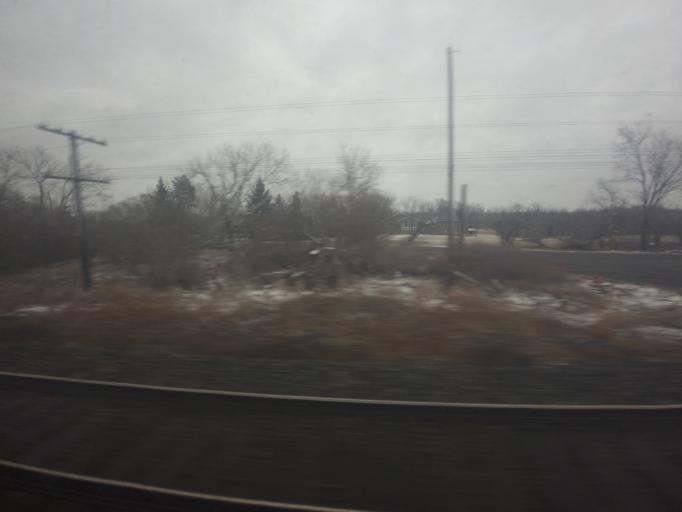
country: CA
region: Ontario
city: Gananoque
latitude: 44.3497
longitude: -76.2589
